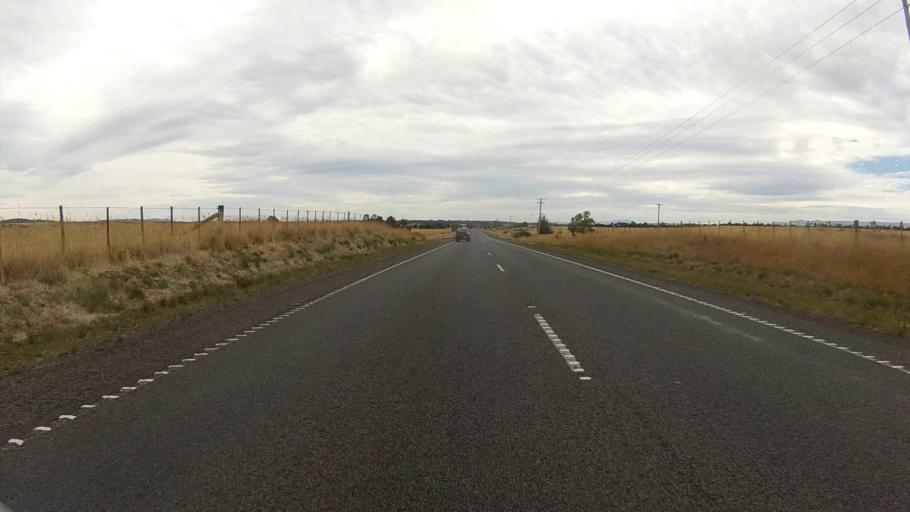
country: AU
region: Tasmania
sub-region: Northern Midlands
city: Evandale
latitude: -41.8625
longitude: 147.4565
